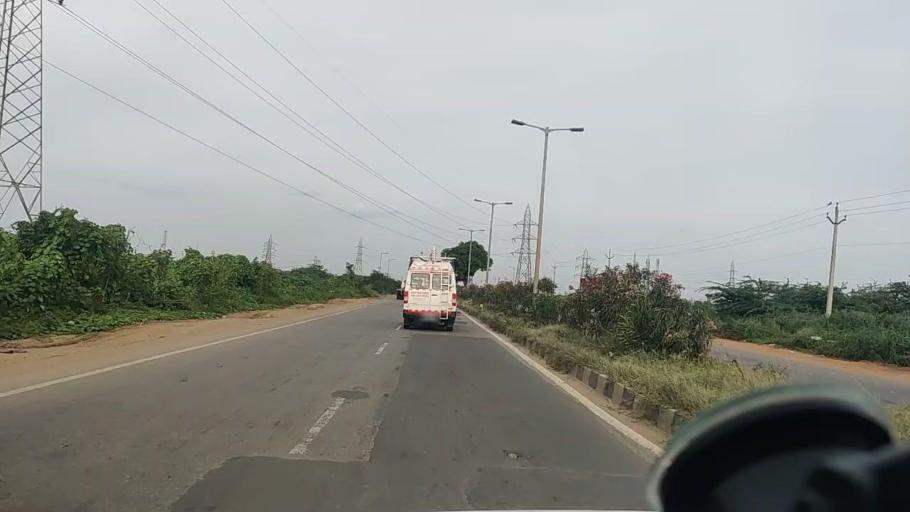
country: IN
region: Tamil Nadu
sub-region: Thiruvallur
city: Manali
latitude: 13.1817
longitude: 80.2657
